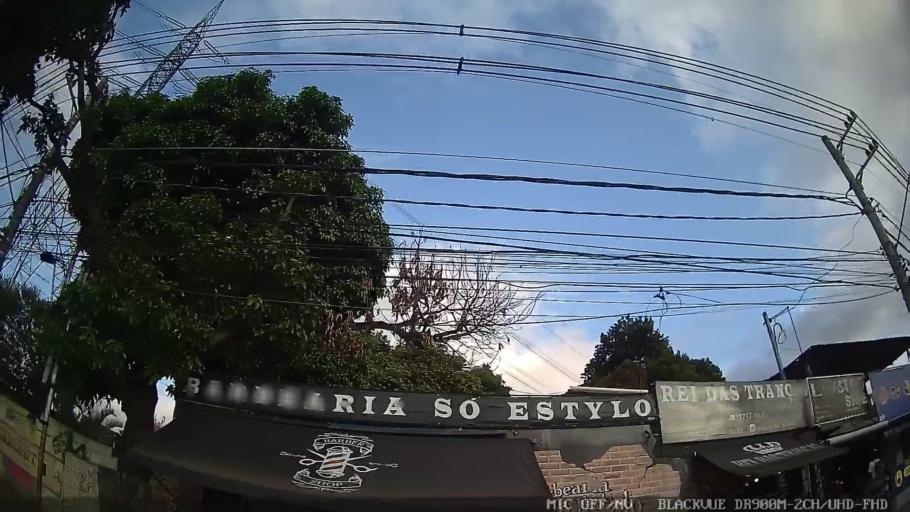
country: BR
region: Sao Paulo
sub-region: Taboao Da Serra
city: Taboao da Serra
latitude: -23.6098
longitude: -46.7521
